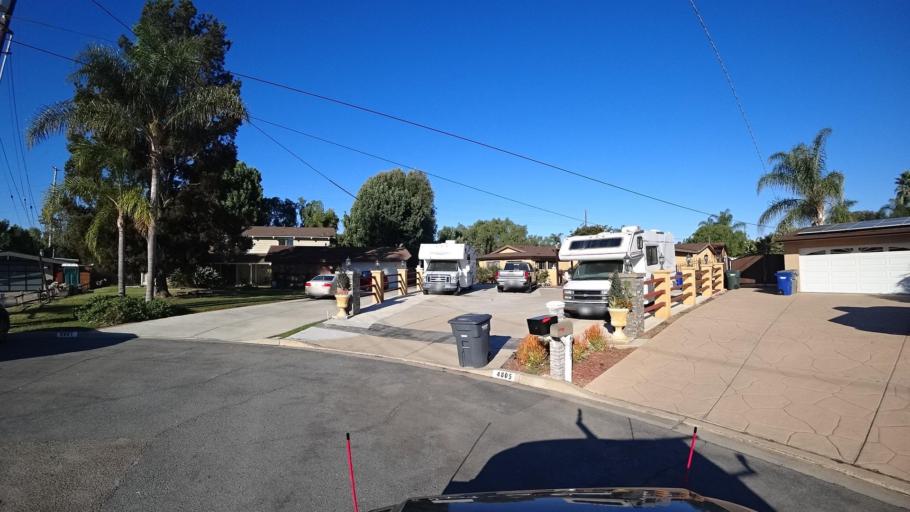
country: US
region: California
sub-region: San Diego County
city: Bonita
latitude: 32.6694
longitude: -117.0271
